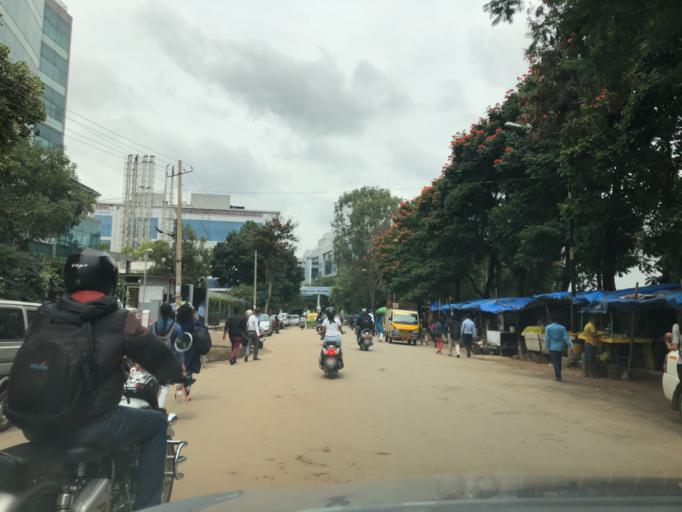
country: IN
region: Karnataka
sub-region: Bangalore Rural
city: Hoskote
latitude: 12.9820
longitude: 77.7273
